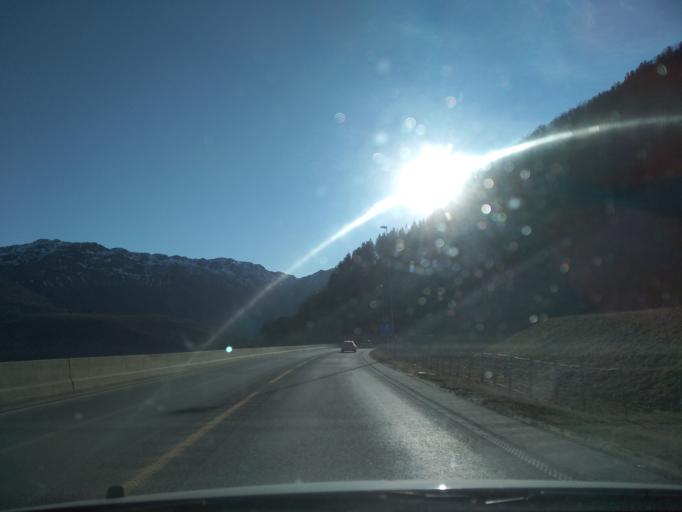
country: NO
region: Hordaland
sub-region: Etne
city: Etne
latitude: 59.7239
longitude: 6.1186
